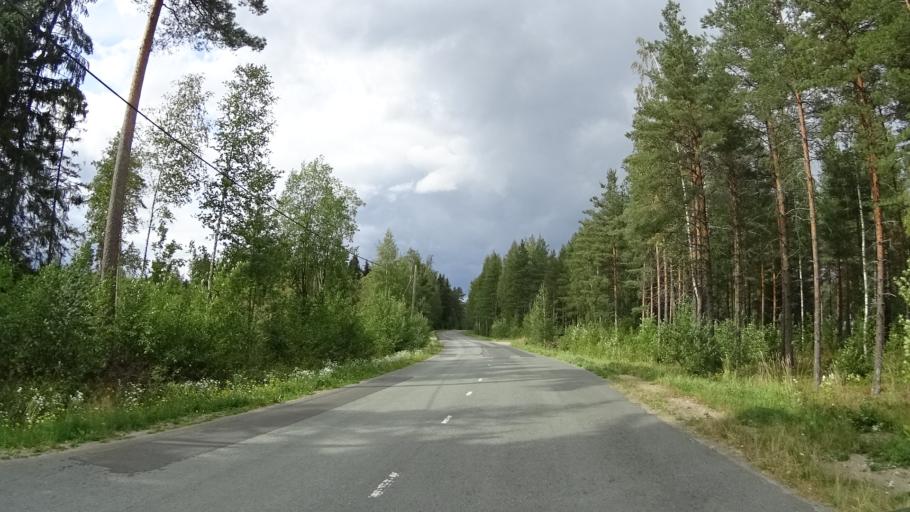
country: FI
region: Pirkanmaa
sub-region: Tampere
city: Kangasala
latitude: 61.4483
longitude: 24.1204
